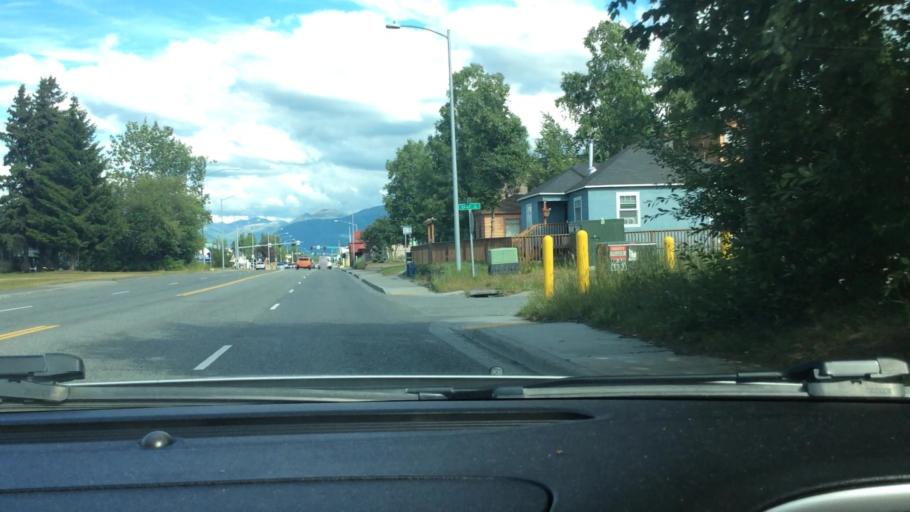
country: US
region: Alaska
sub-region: Anchorage Municipality
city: Anchorage
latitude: 61.2077
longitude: -149.8756
